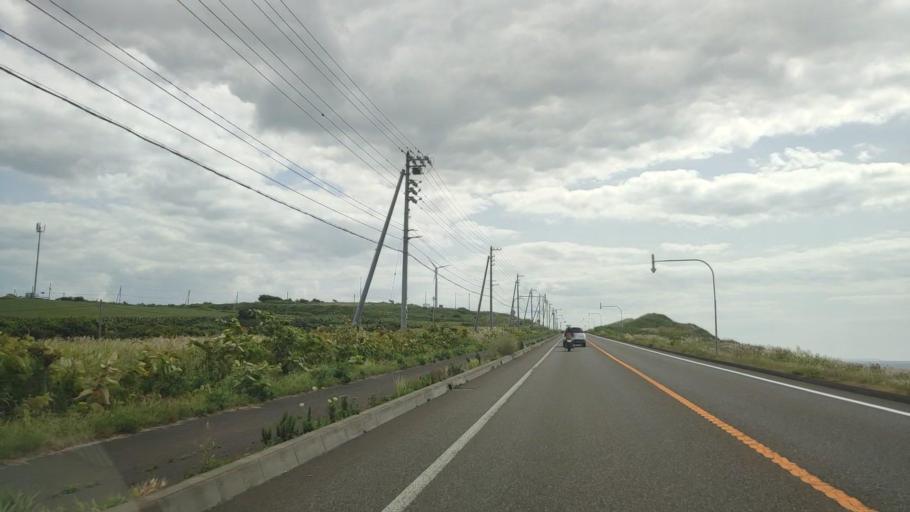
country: JP
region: Hokkaido
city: Rumoi
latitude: 44.5242
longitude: 141.7655
